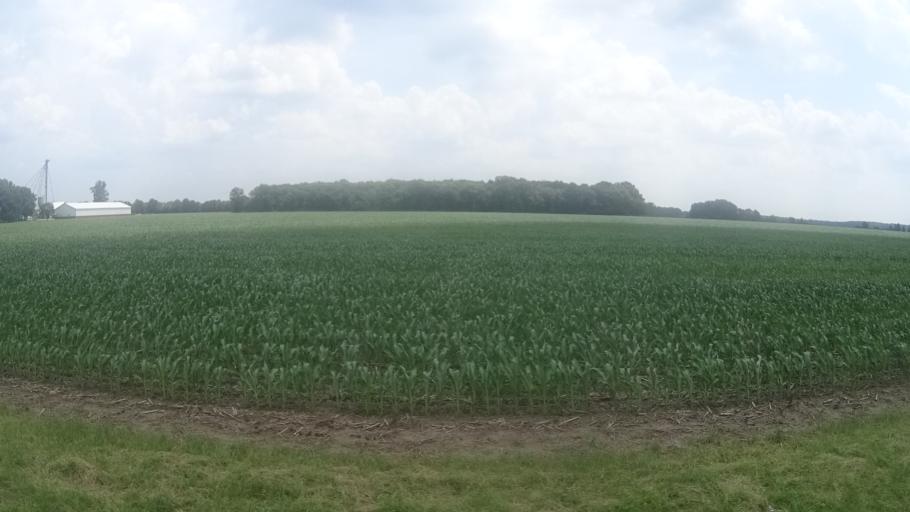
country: US
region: Ohio
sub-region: Huron County
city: Monroeville
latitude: 41.3173
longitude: -82.6929
